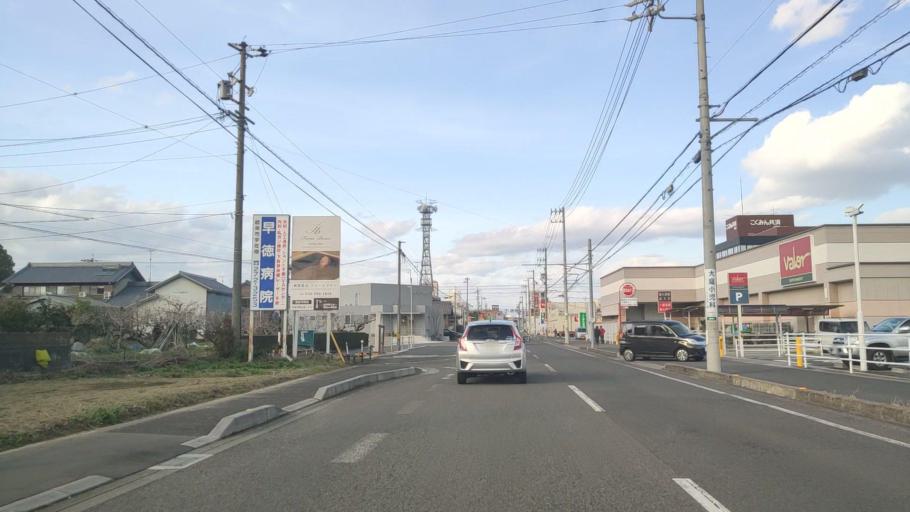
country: JP
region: Gifu
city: Kasamatsucho
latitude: 35.3910
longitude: 136.7547
